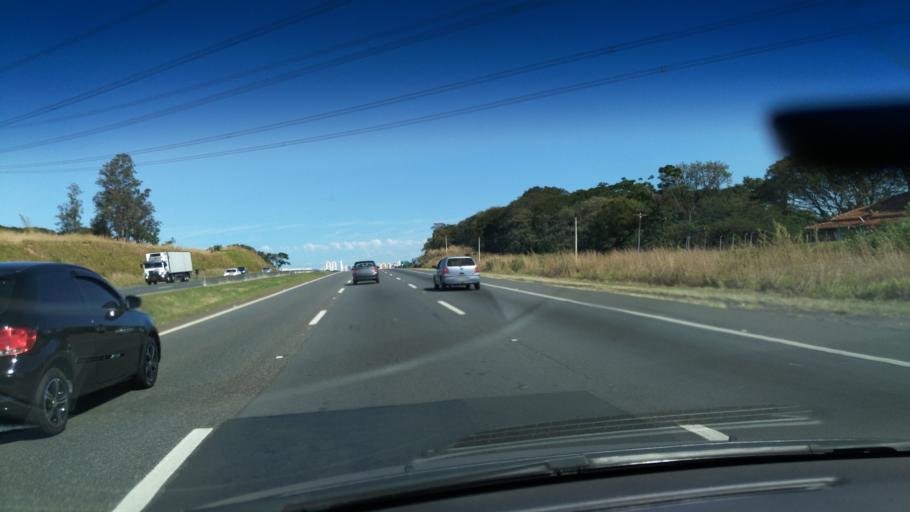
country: BR
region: Sao Paulo
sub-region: Campinas
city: Campinas
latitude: -22.8080
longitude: -47.0336
